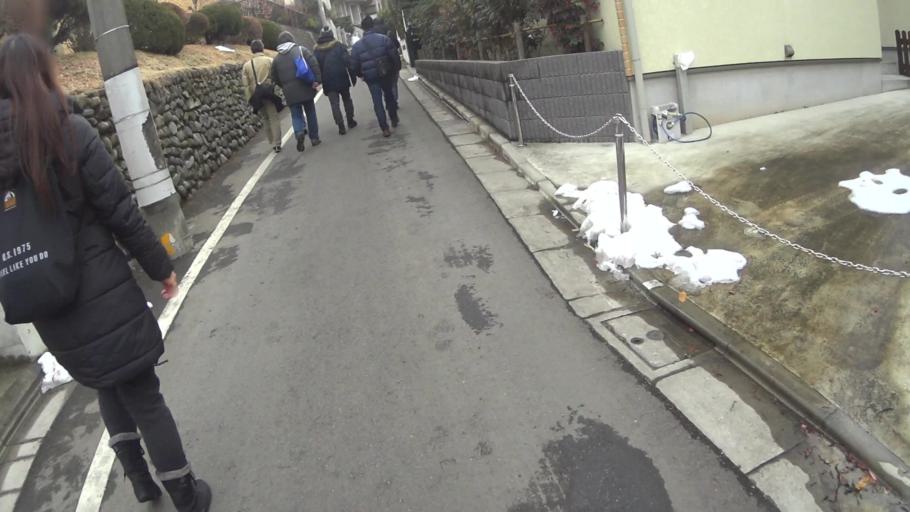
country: JP
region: Tokyo
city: Musashino
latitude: 35.7337
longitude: 139.5993
